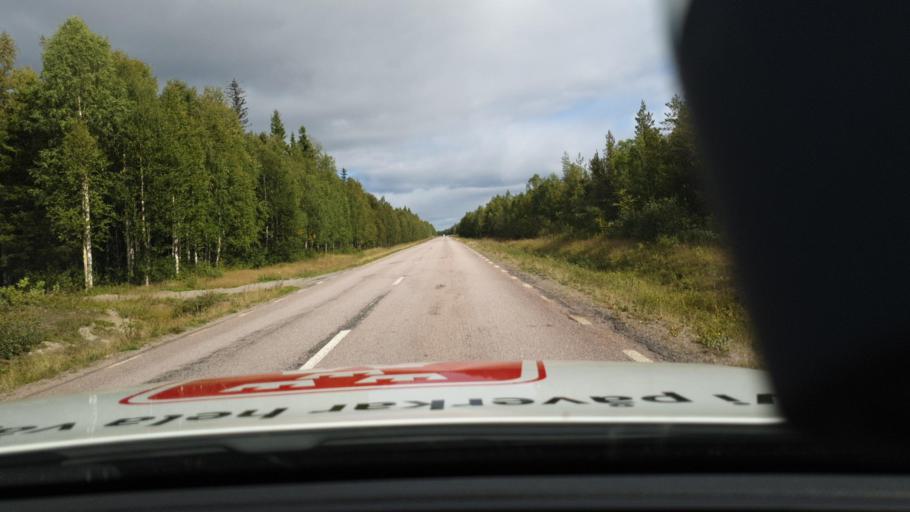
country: SE
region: Norrbotten
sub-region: Pajala Kommun
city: Pajala
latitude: 67.1904
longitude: 22.7404
